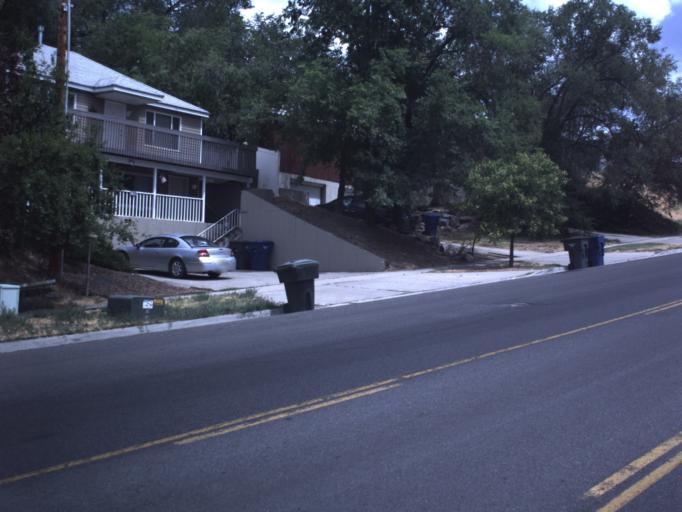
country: US
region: Utah
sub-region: Weber County
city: Ogden
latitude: 41.2101
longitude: -111.9621
